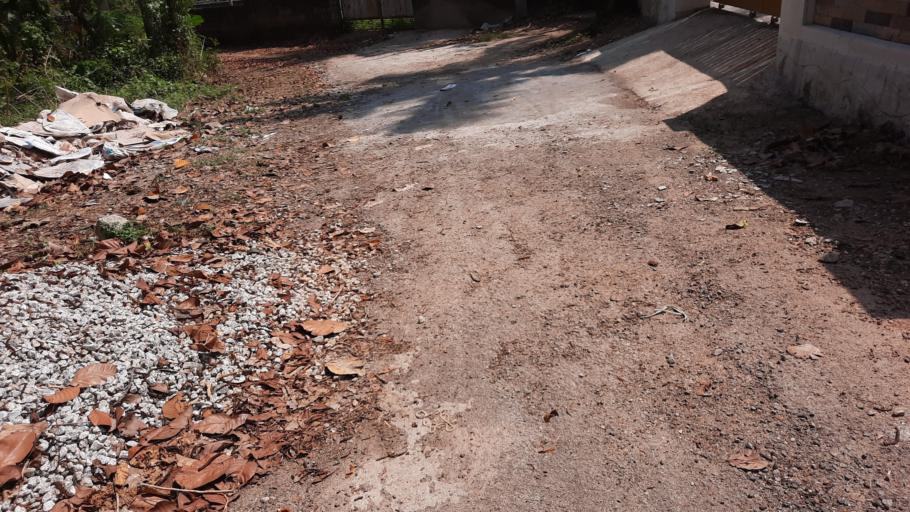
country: IN
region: Kerala
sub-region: Thiruvananthapuram
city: Thiruvananthapuram
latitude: 8.5567
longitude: 76.9319
